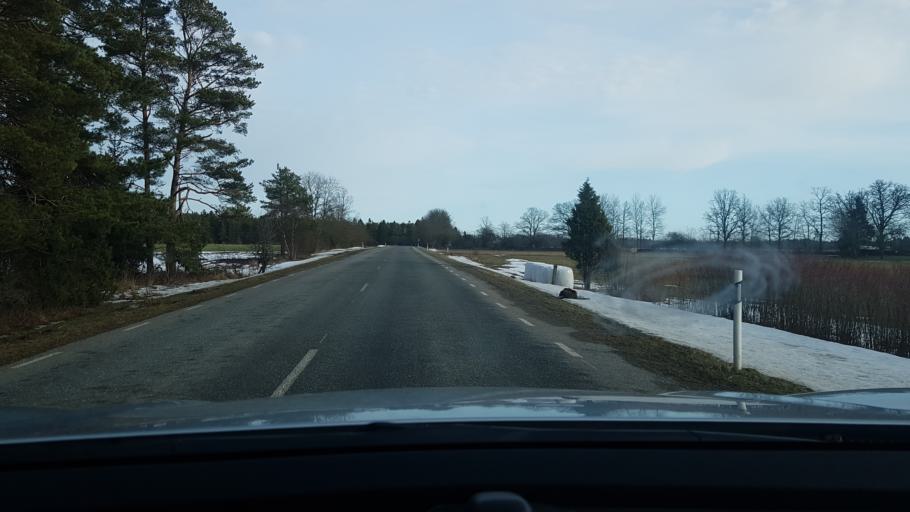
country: EE
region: Saare
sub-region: Kuressaare linn
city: Kuressaare
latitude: 58.4065
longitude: 22.6494
